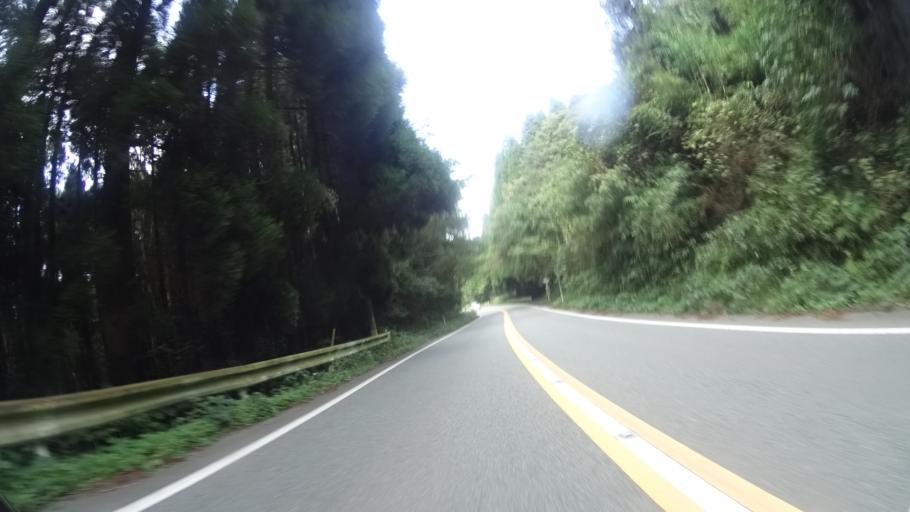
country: JP
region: Kumamoto
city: Aso
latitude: 33.0691
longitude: 131.0643
